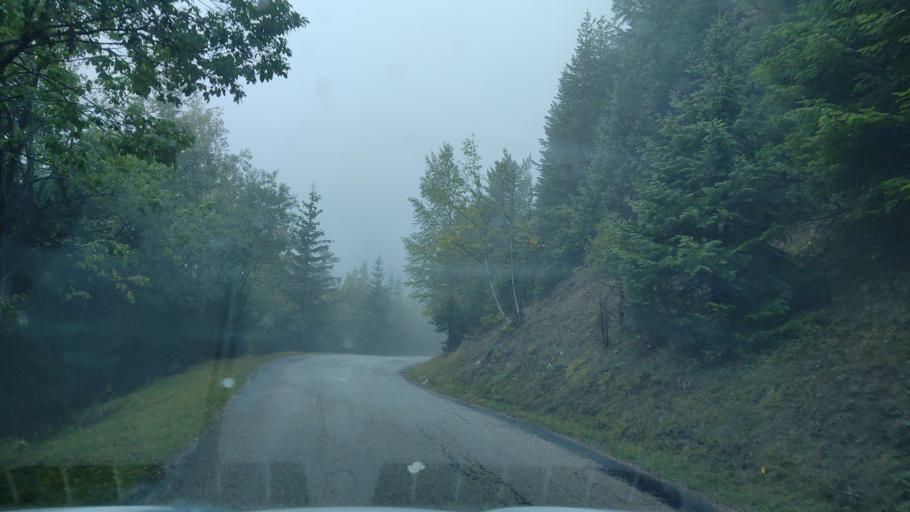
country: FR
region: Rhone-Alpes
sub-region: Departement de la Savoie
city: Modane
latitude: 45.3015
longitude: 6.8228
